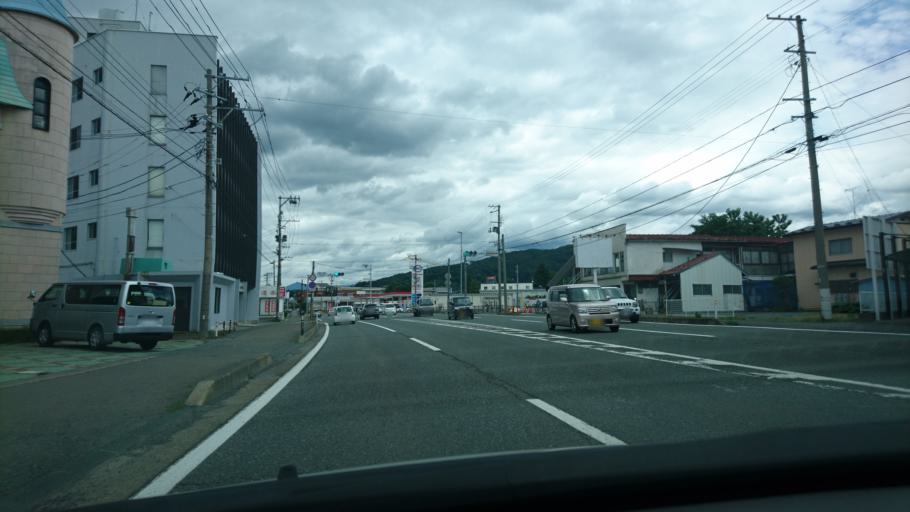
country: JP
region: Iwate
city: Morioka-shi
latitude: 39.6874
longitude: 141.1643
